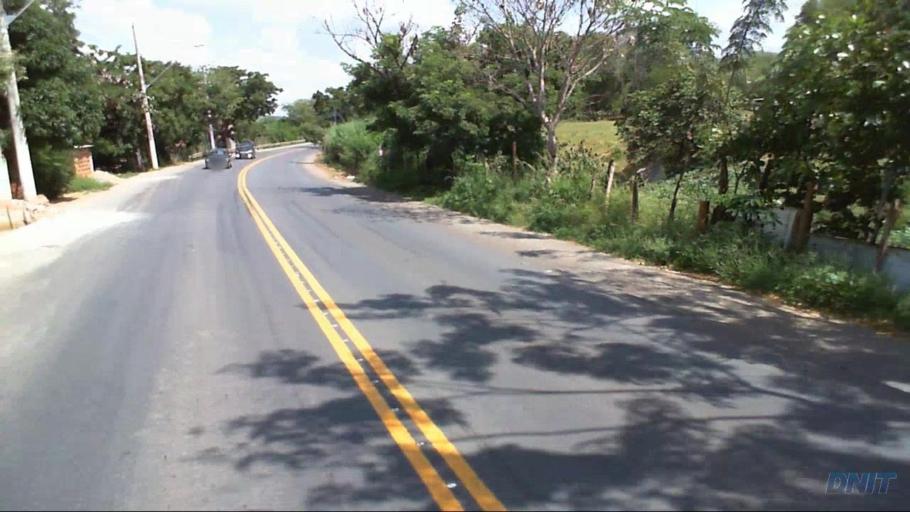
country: BR
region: Minas Gerais
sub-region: Governador Valadares
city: Governador Valadares
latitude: -18.9139
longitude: -41.9985
